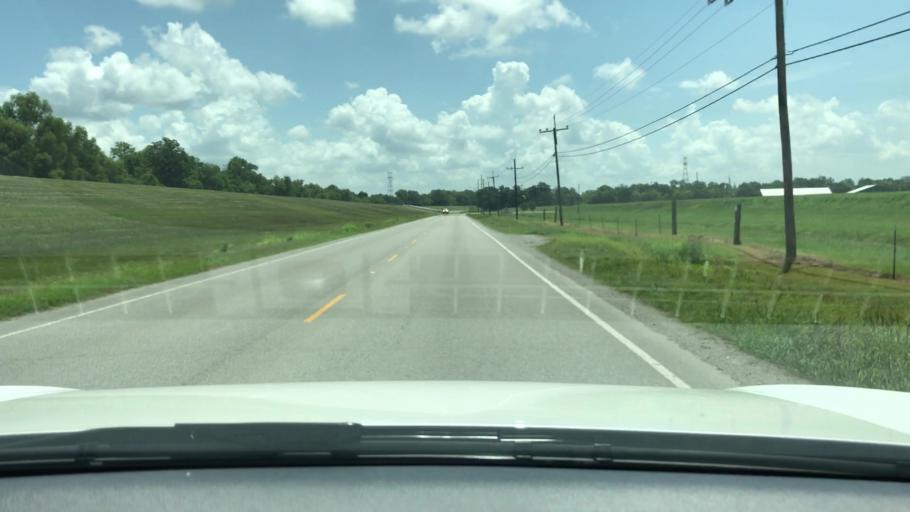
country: US
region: Louisiana
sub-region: Iberville Parish
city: Saint Gabriel
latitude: 30.2714
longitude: -91.1511
